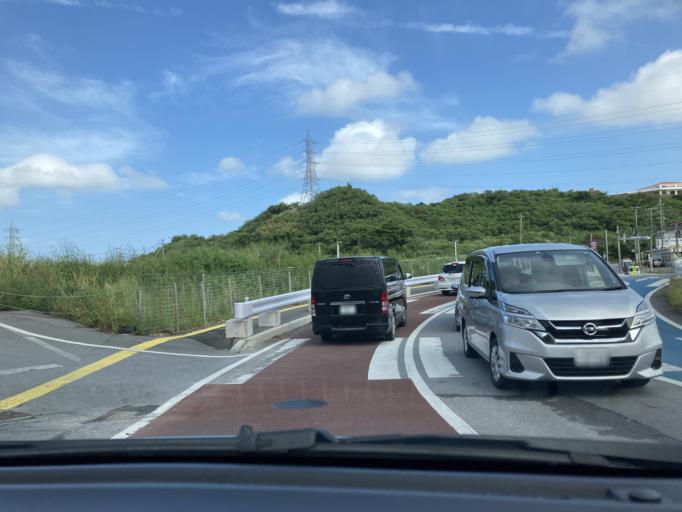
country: JP
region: Okinawa
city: Ginowan
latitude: 26.2393
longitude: 127.7490
